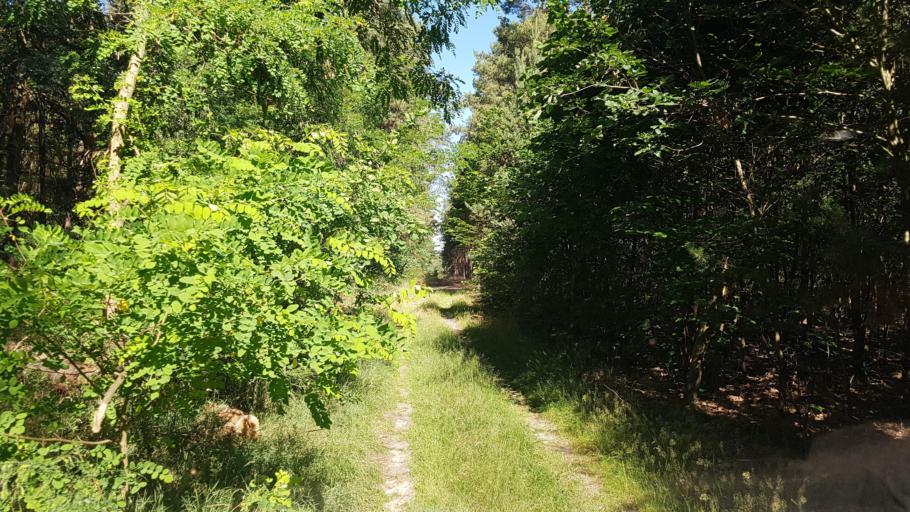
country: DE
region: Brandenburg
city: Juterbog
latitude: 51.9785
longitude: 13.1392
